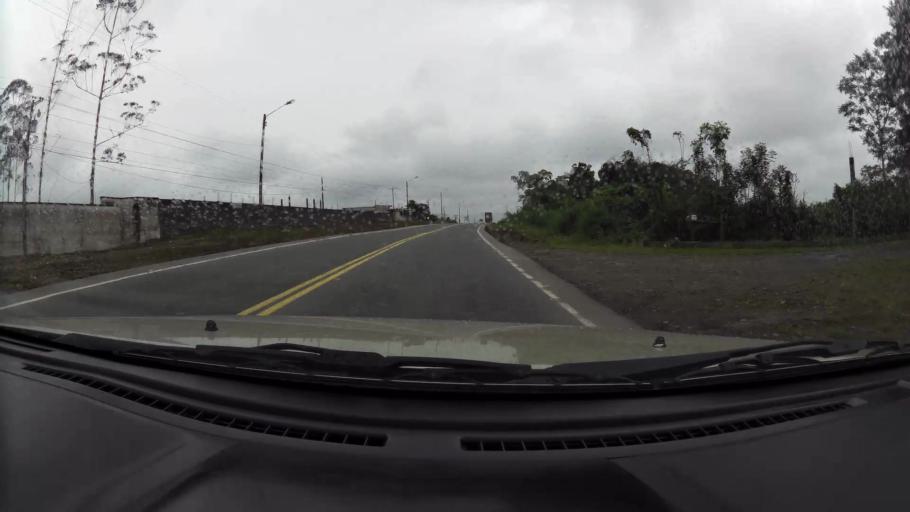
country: EC
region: Santo Domingo de los Tsachilas
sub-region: Canton Santo Domingo de los Colorados
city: Santo Domingo de los Colorados
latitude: -0.2701
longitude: -79.1476
